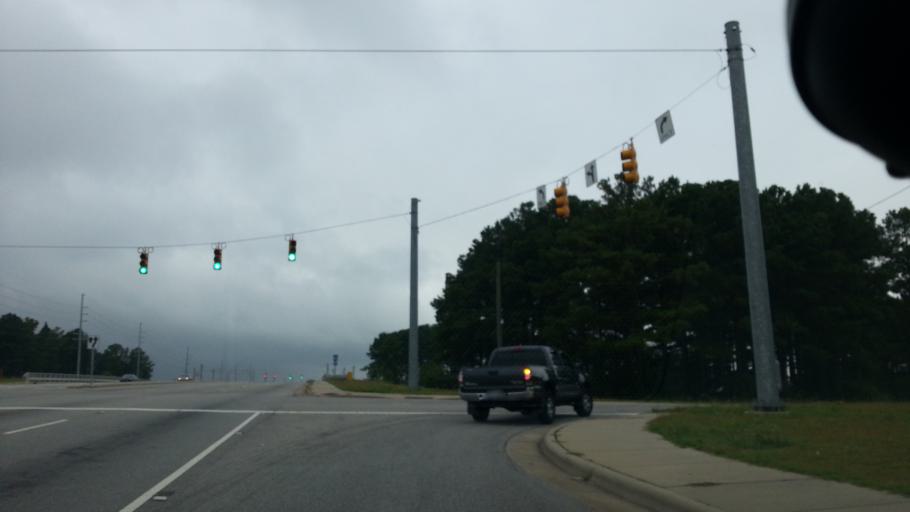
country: US
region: North Carolina
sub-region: Cumberland County
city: Fayetteville
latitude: 35.0682
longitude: -78.9546
